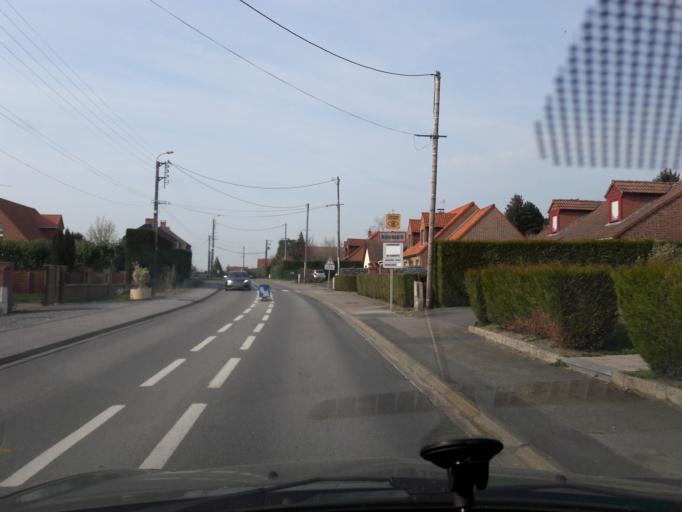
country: FR
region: Nord-Pas-de-Calais
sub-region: Departement du Nord
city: Rousies
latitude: 50.2635
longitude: 4.0082
